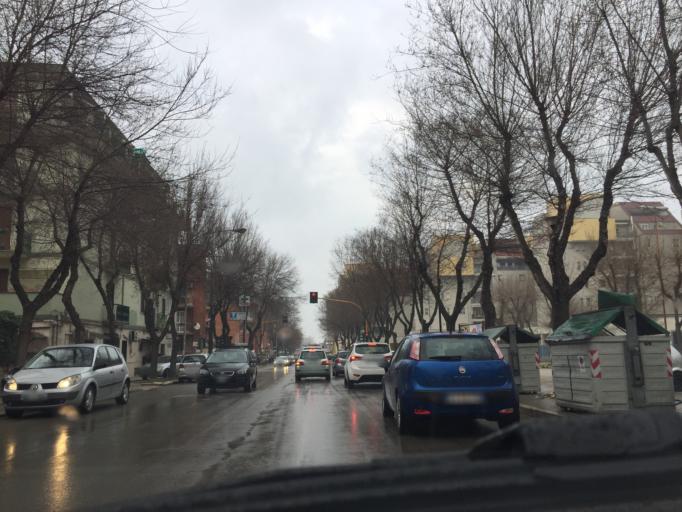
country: IT
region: Apulia
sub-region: Provincia di Foggia
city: Foggia
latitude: 41.4677
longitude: 15.5363
